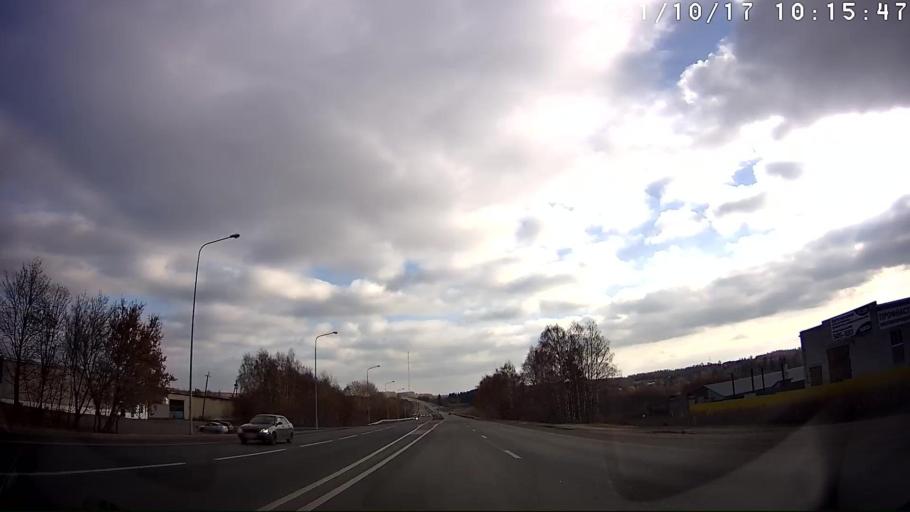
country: RU
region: Mariy-El
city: Sovetskiy
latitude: 56.7519
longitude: 48.4856
